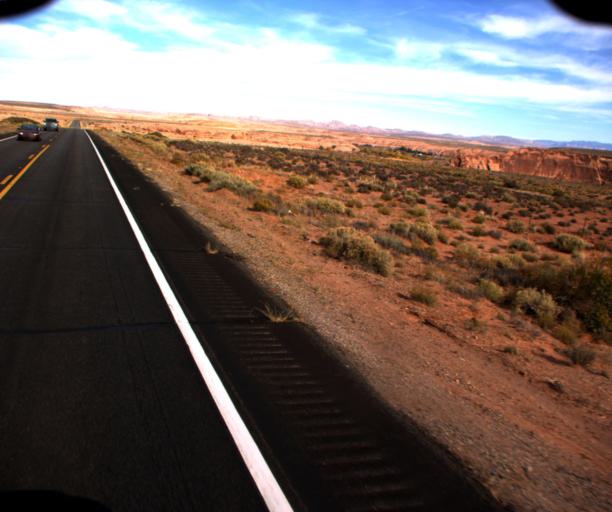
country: US
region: Arizona
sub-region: Navajo County
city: Kayenta
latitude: 36.9404
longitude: -109.7329
